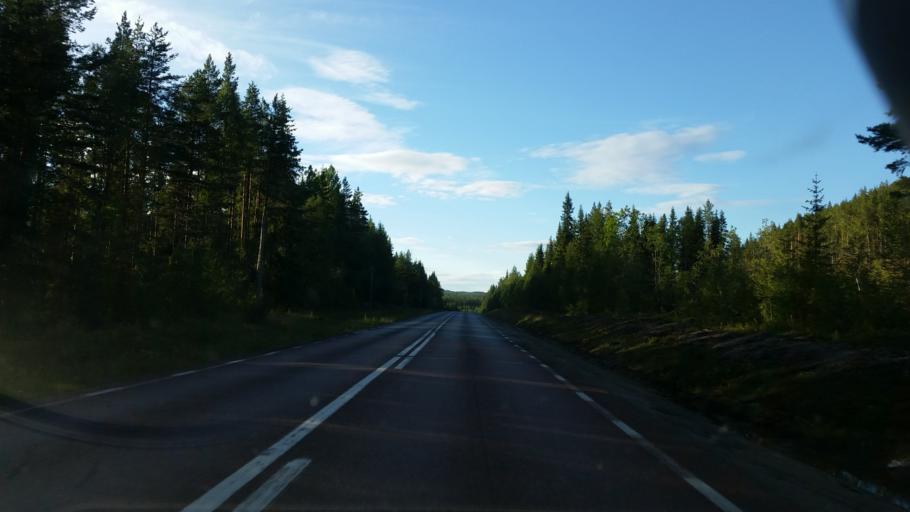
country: SE
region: Vaesterbotten
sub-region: Dorotea Kommun
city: Dorotea
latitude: 64.2013
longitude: 16.2874
